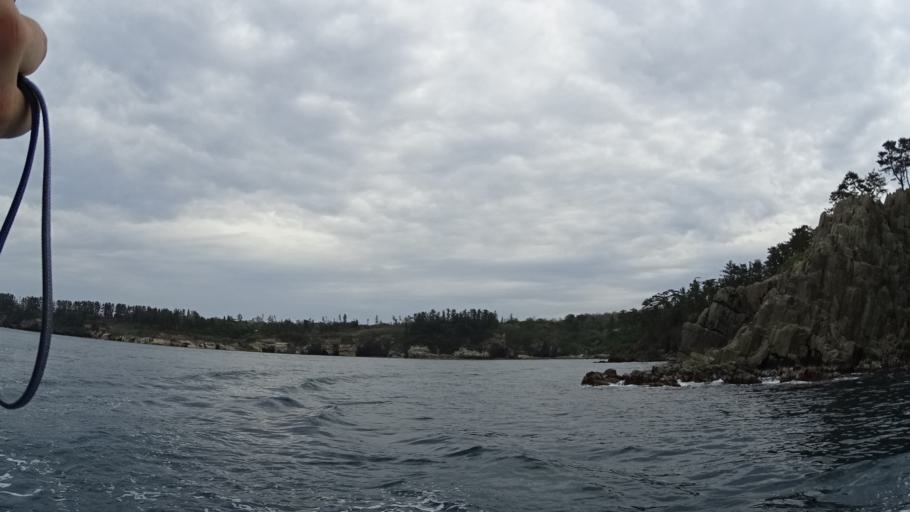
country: JP
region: Fukui
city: Mikuni
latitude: 36.2387
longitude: 136.1257
